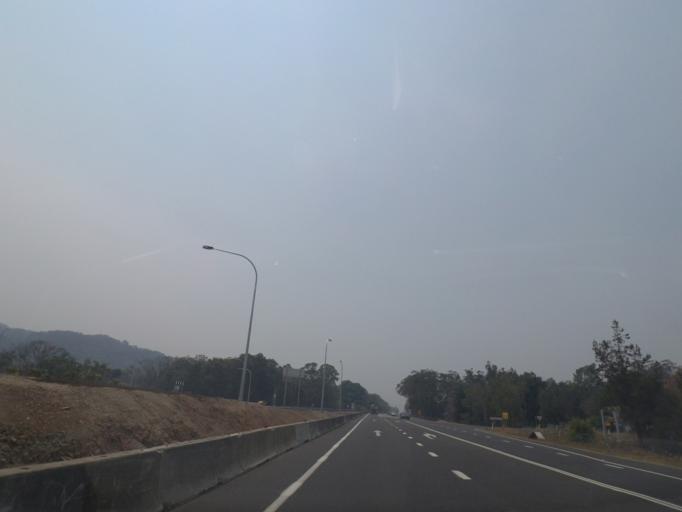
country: AU
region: New South Wales
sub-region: Ballina
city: Ballina
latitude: -28.9228
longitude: 153.4760
